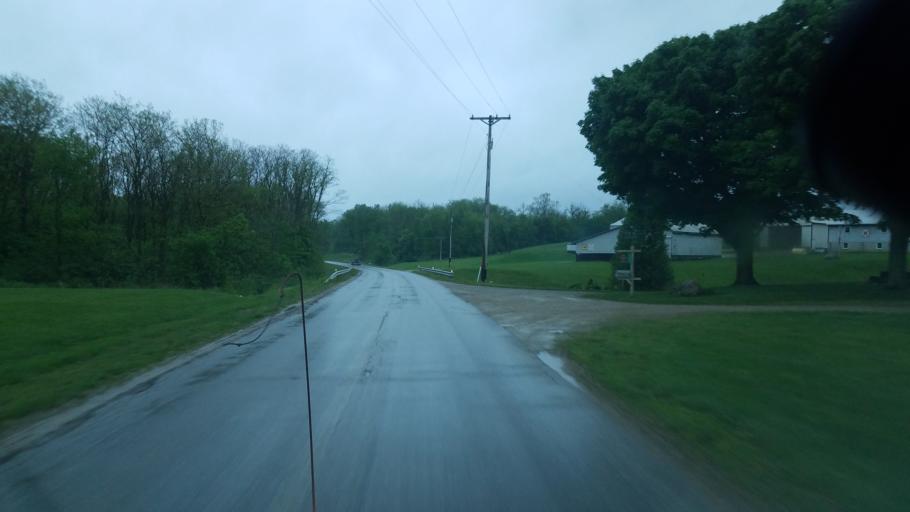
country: US
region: Ohio
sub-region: Highland County
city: Greenfield
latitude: 39.2962
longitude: -83.4633
